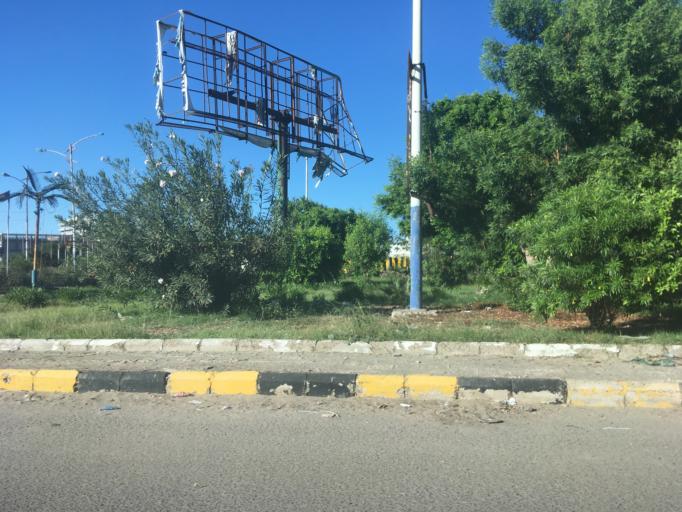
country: YE
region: Aden
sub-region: Craiter
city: Aden
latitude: 12.7921
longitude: 45.0378
